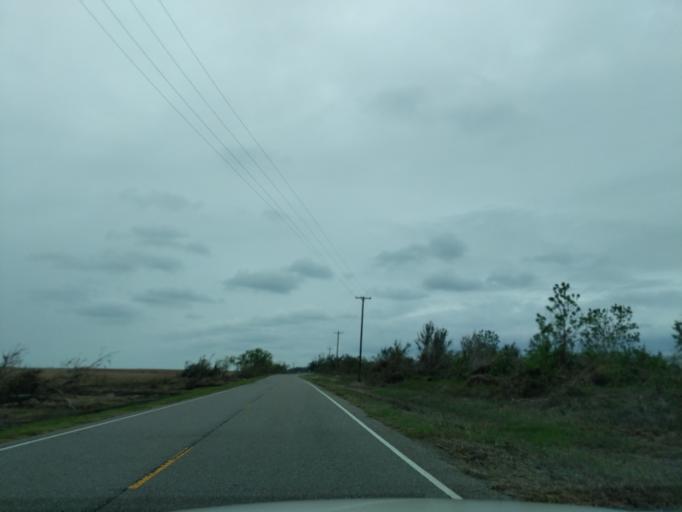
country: US
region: Louisiana
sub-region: Cameron Parish
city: Cameron
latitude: 29.7864
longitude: -93.1725
